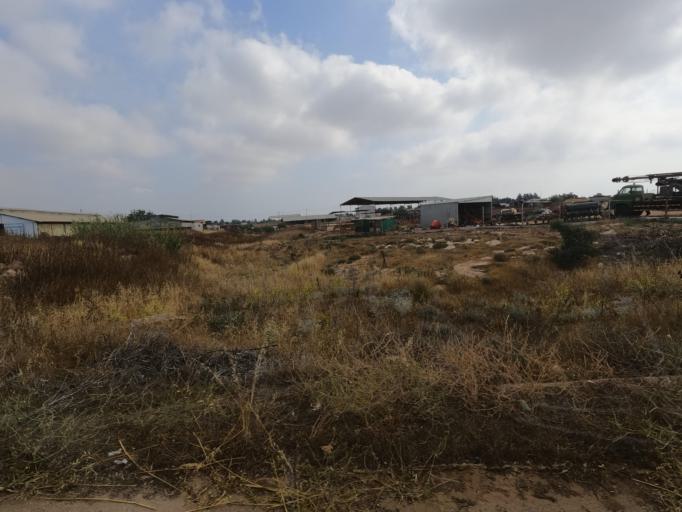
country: CY
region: Ammochostos
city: Frenaros
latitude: 35.0586
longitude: 33.9375
